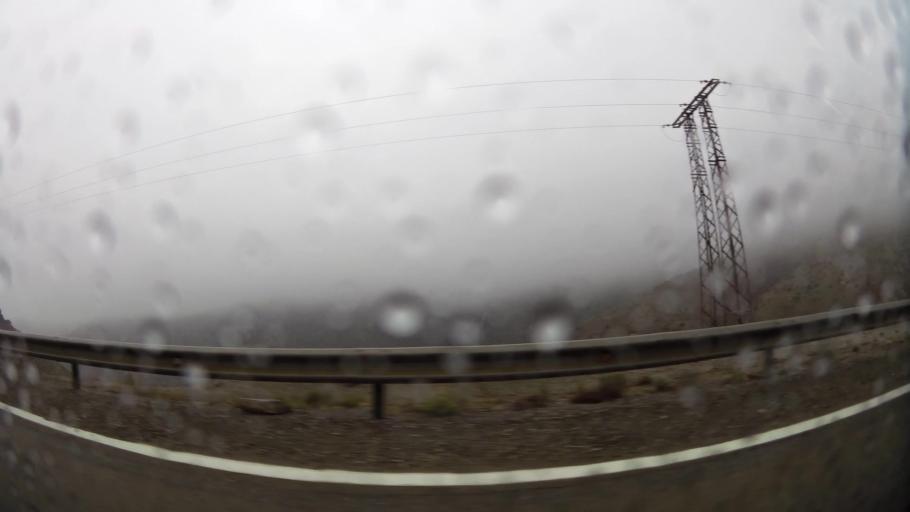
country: MA
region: Taza-Al Hoceima-Taounate
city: Tirhanimine
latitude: 35.2369
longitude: -3.9694
